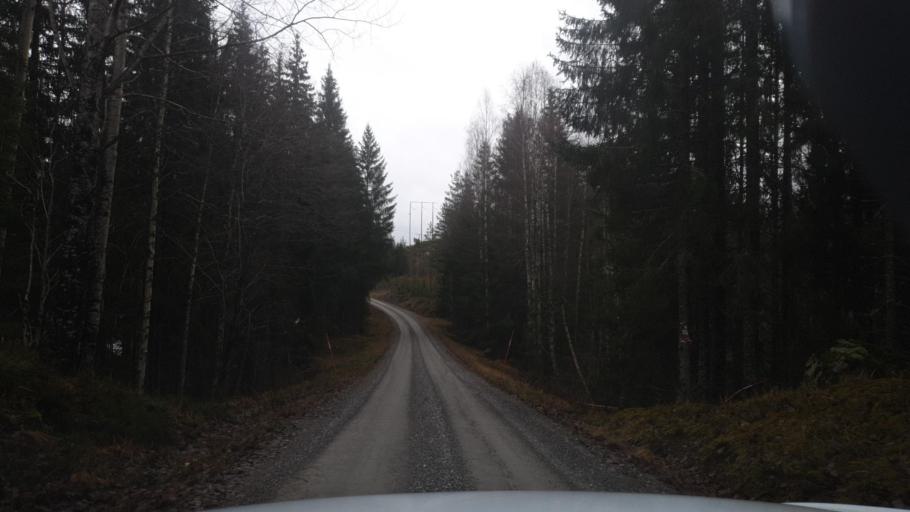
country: SE
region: Vaermland
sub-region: Arvika Kommun
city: Arvika
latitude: 59.5377
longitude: 12.4460
